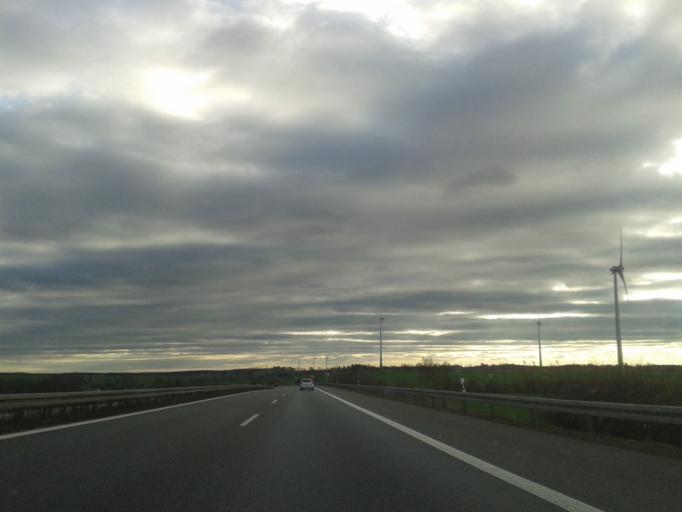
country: DE
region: Saxony
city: Wachau
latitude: 51.1645
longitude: 13.9230
